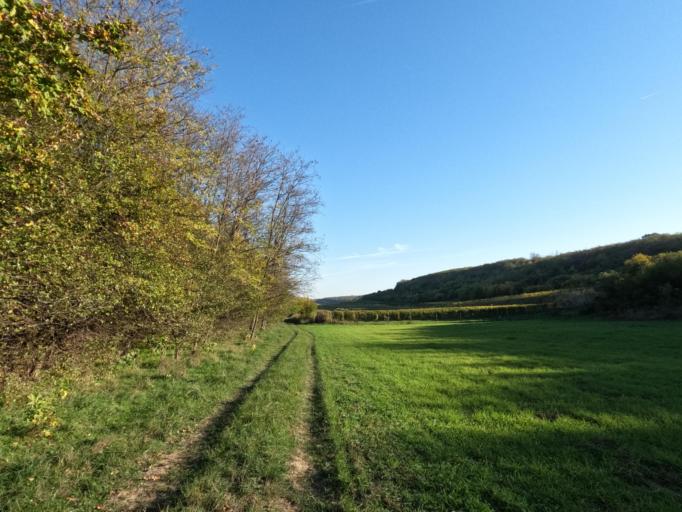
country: HU
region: Tolna
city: Szekszard
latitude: 46.3049
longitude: 18.6569
